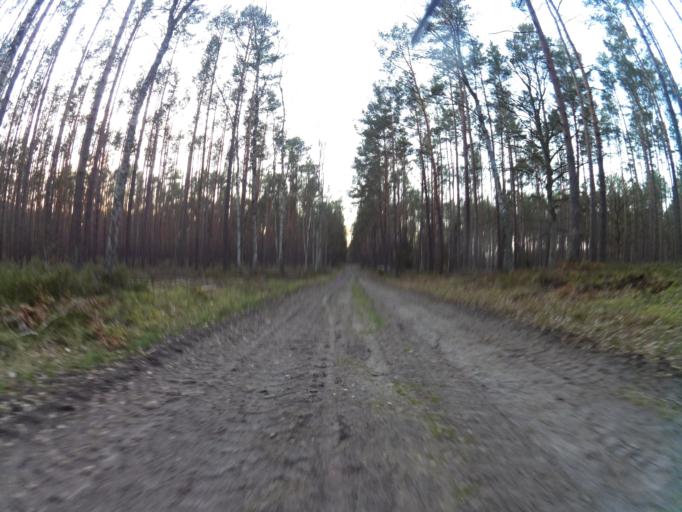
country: PL
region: West Pomeranian Voivodeship
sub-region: Powiat policki
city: Nowe Warpno
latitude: 53.6912
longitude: 14.3295
